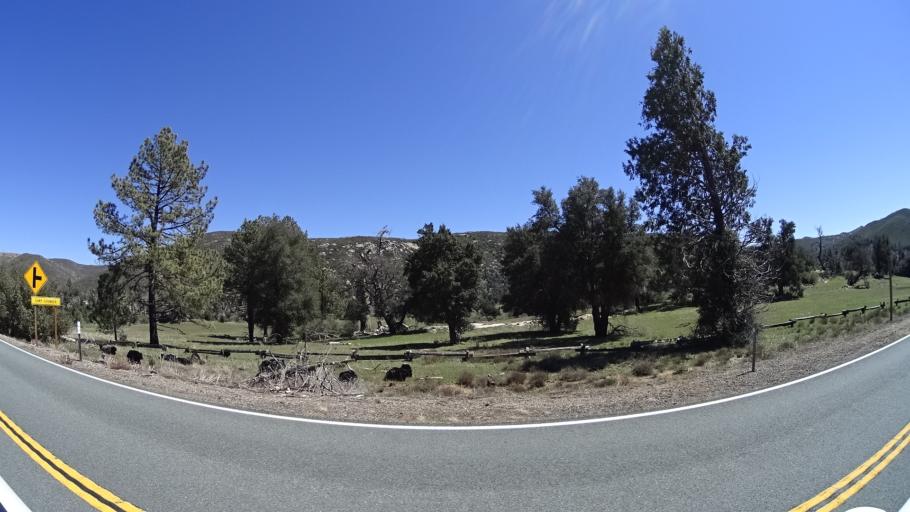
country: US
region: California
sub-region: San Diego County
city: Descanso
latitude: 32.9250
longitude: -116.5641
